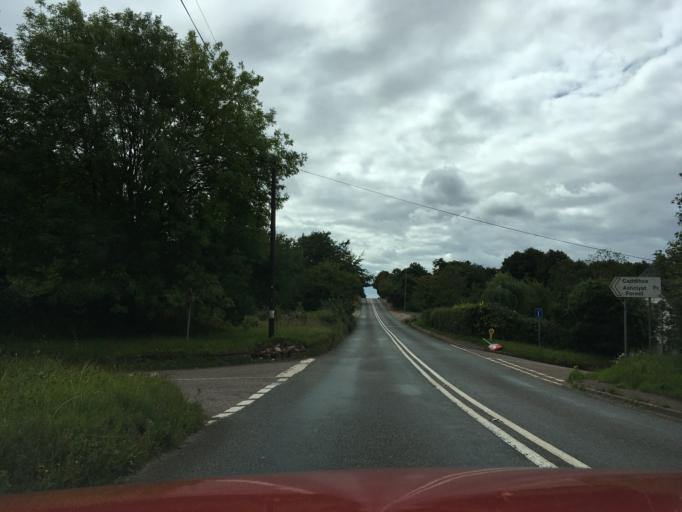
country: GB
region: England
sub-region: Devon
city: Bradninch
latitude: 50.7923
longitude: -3.4418
